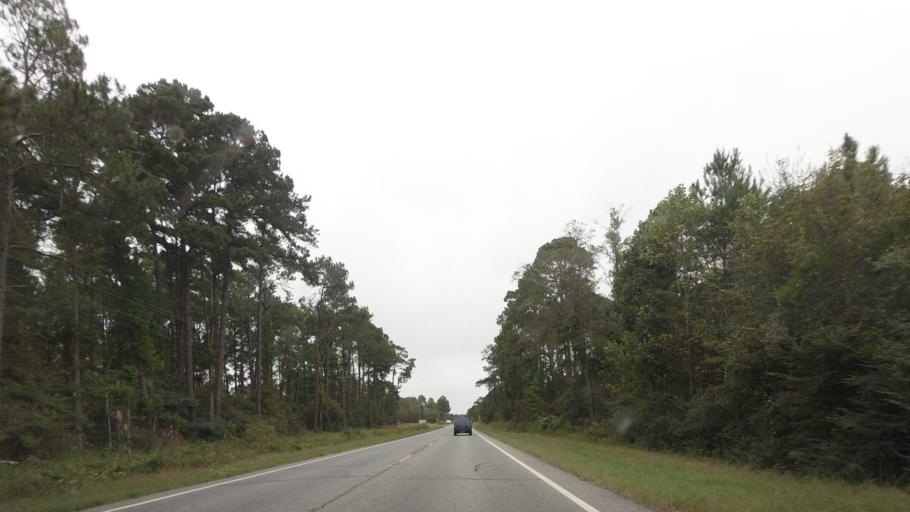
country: US
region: Georgia
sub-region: Irwin County
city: Ocilla
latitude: 31.5632
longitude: -83.2529
